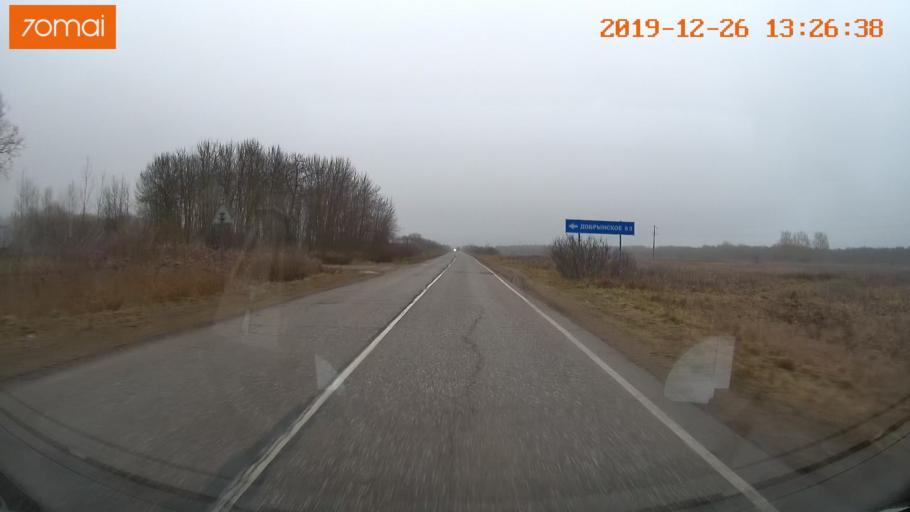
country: RU
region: Vologda
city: Cherepovets
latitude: 58.8617
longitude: 38.2289
